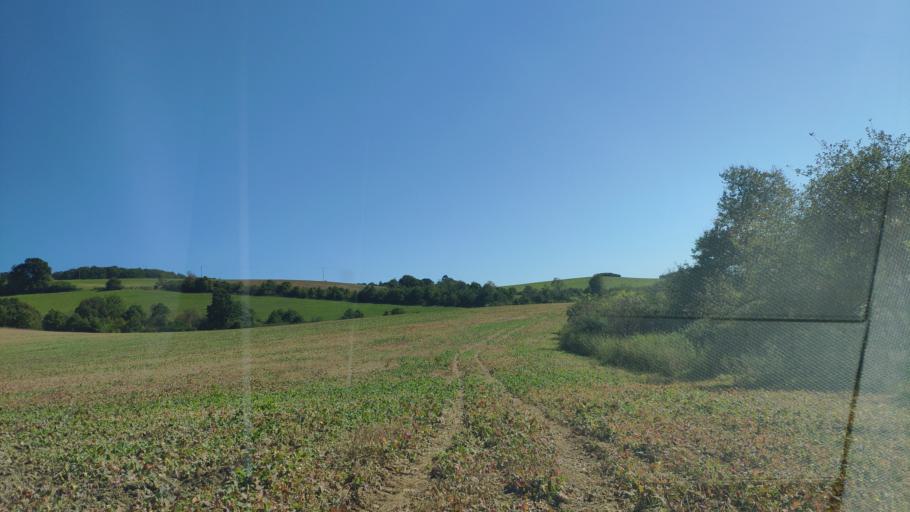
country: SK
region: Presovsky
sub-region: Okres Presov
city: Presov
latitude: 48.9656
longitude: 21.1402
